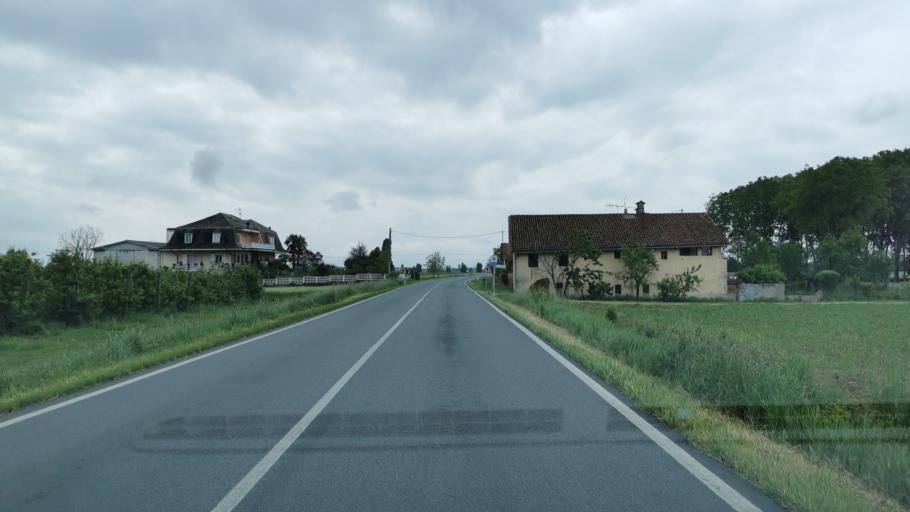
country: IT
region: Piedmont
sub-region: Provincia di Cuneo
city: Villafalletto
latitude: 44.5712
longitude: 7.5289
